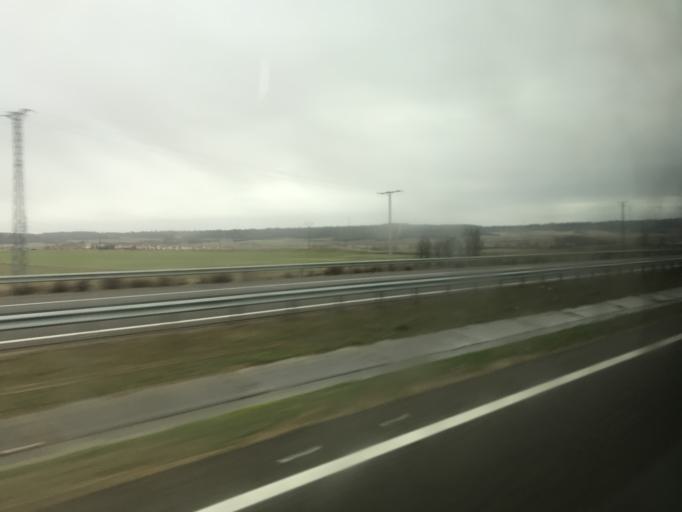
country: ES
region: Castille and Leon
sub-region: Provincia de Palencia
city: Villalobon
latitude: 42.0308
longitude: -4.5169
